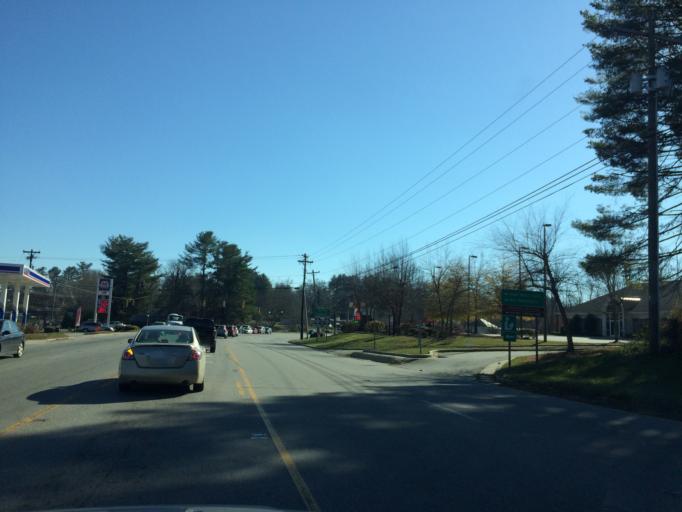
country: US
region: North Carolina
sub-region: Henderson County
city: Mills River
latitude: 35.3892
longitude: -82.5674
